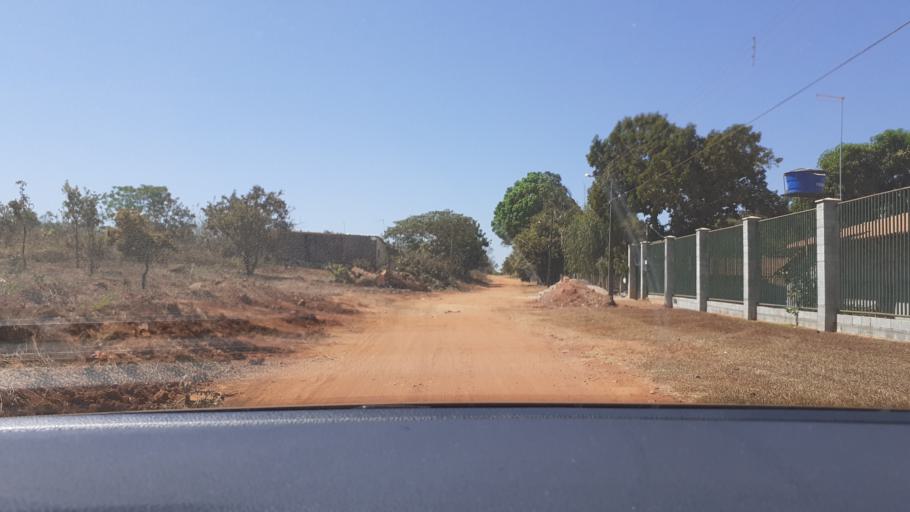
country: BR
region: Goias
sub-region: Aparecida De Goiania
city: Aparecida de Goiania
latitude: -16.8774
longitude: -49.2758
